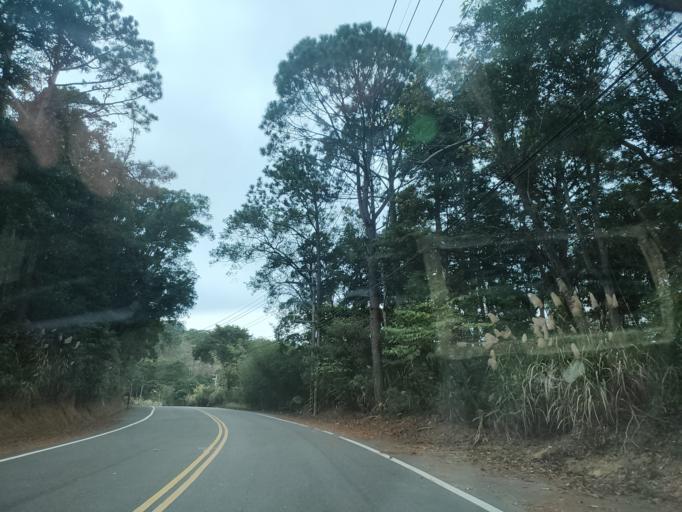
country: TW
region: Taiwan
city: Fengyuan
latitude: 24.3650
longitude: 120.7771
